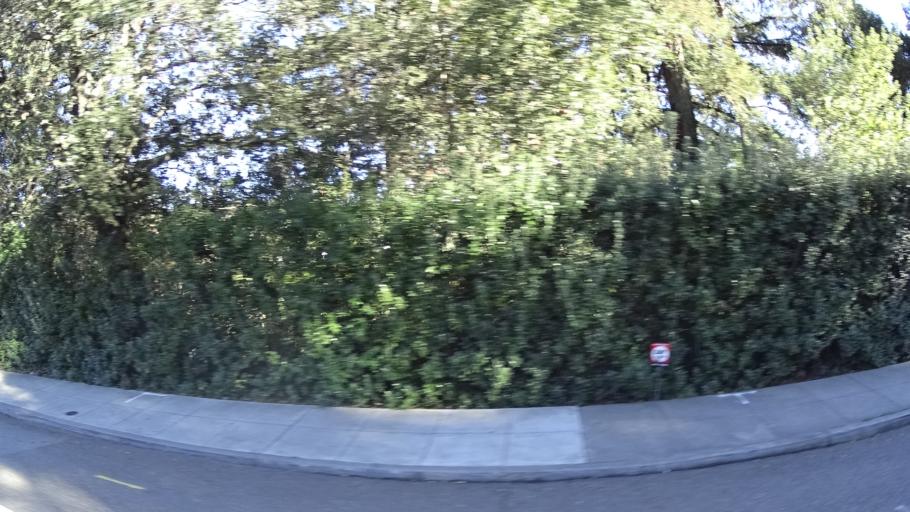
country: US
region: California
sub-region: Alameda County
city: Piedmont
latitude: 37.8151
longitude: -122.2218
